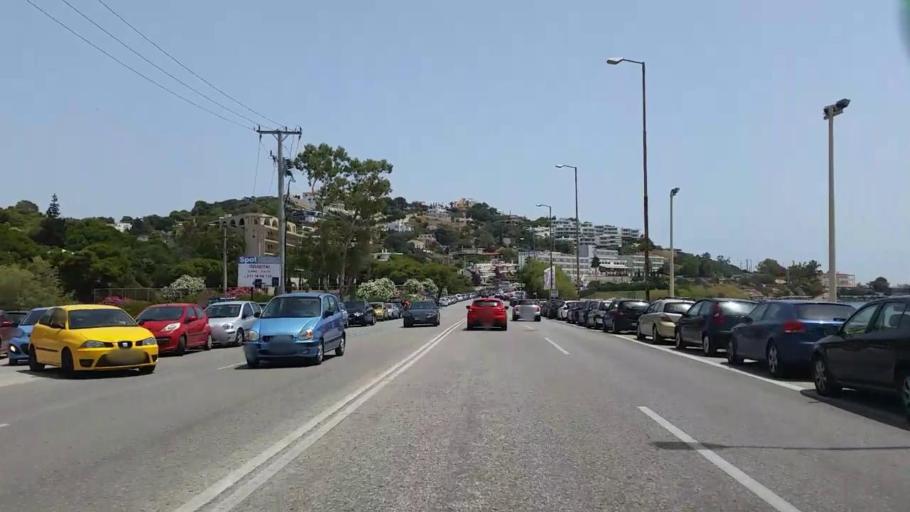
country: GR
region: Attica
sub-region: Nomarchia Anatolikis Attikis
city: Saronida
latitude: 37.7291
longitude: 23.9065
